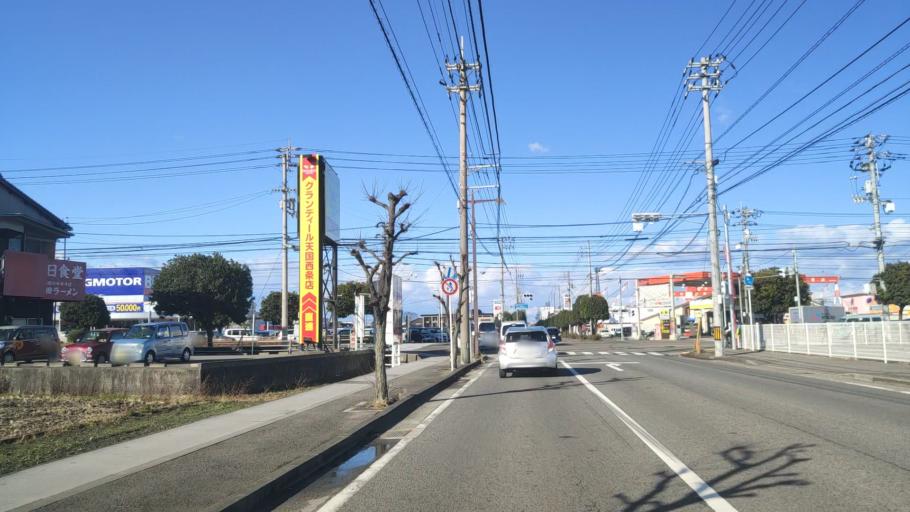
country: JP
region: Ehime
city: Saijo
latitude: 33.9289
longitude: 133.1903
